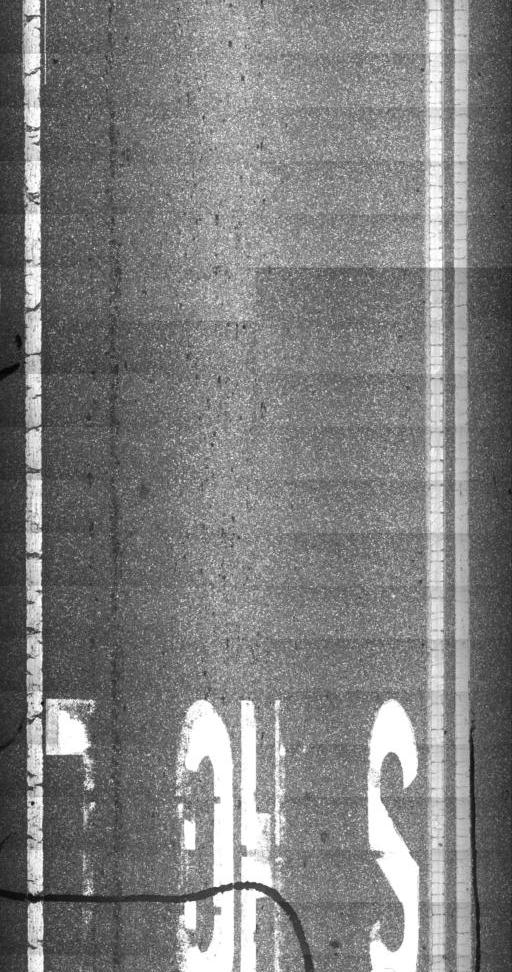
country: US
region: New Hampshire
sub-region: Grafton County
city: Hanover
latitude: 43.7122
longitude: -72.3079
